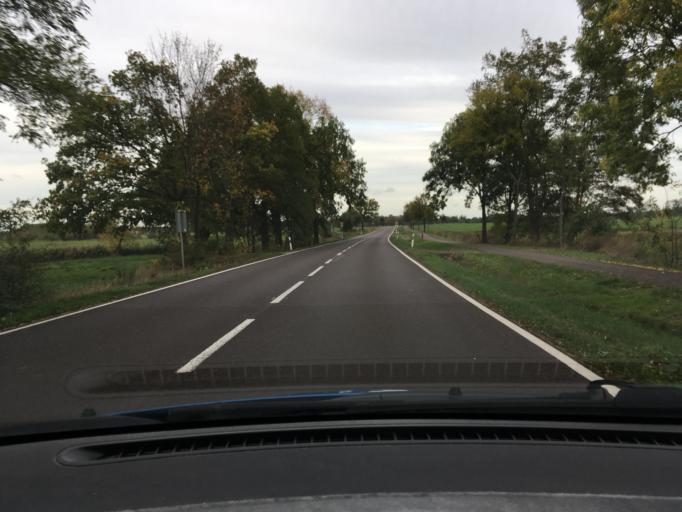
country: DE
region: Saxony-Anhalt
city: Wahlitz
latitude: 52.1199
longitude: 11.7638
